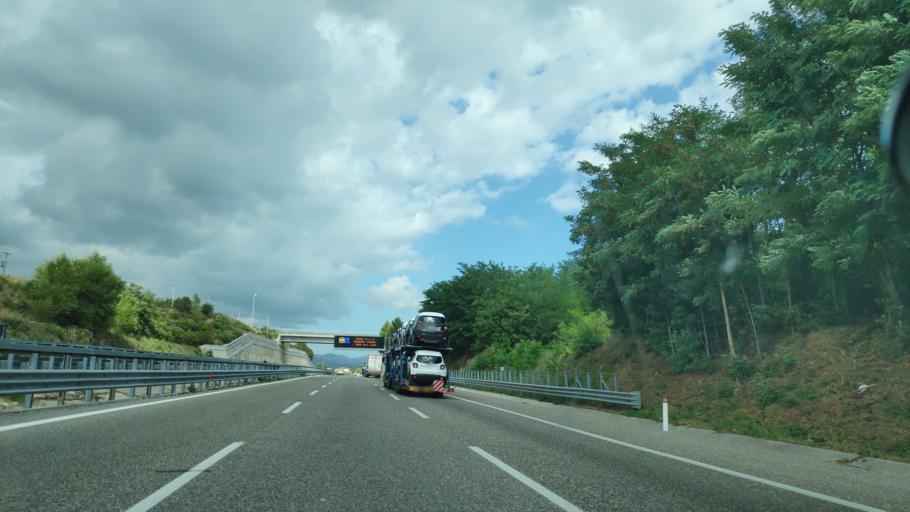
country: IT
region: Campania
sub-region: Provincia di Salerno
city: Contursi Terme
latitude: 40.6142
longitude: 15.2663
